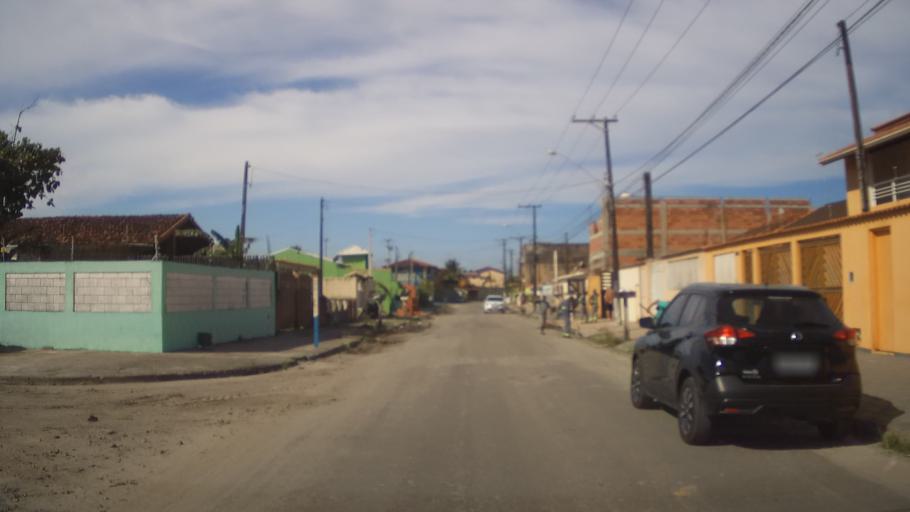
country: BR
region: Sao Paulo
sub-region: Itanhaem
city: Itanhaem
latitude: -24.2064
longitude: -46.8359
